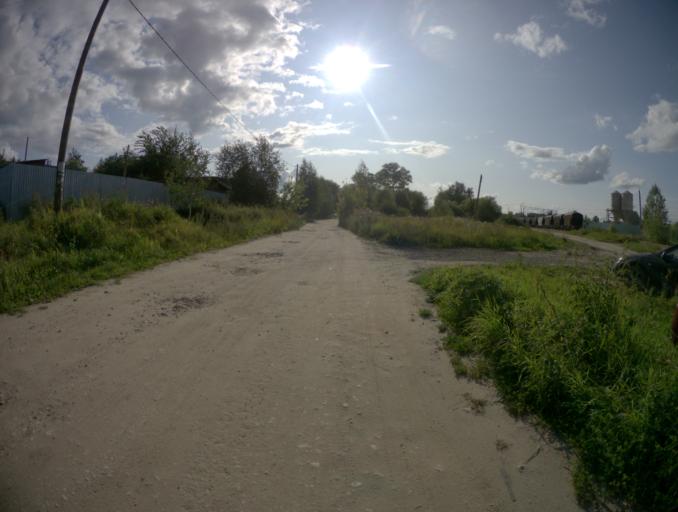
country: RU
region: Vladimir
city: Lakinsk
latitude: 56.0197
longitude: 39.9888
